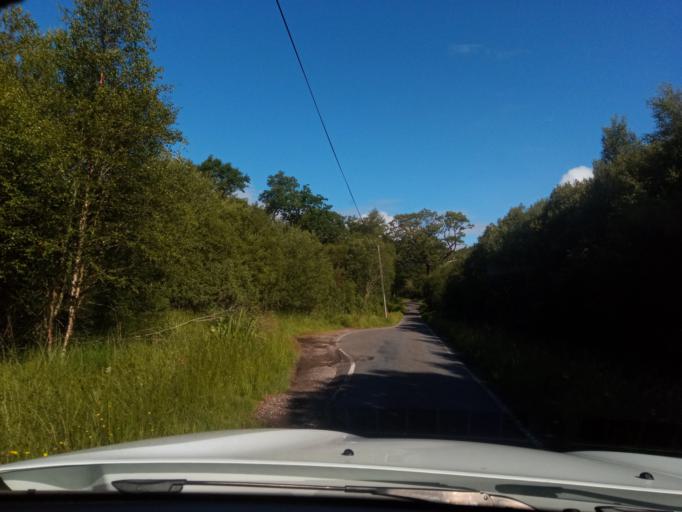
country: GB
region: Scotland
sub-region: Argyll and Bute
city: Isle Of Mull
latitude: 56.6959
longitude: -5.6843
